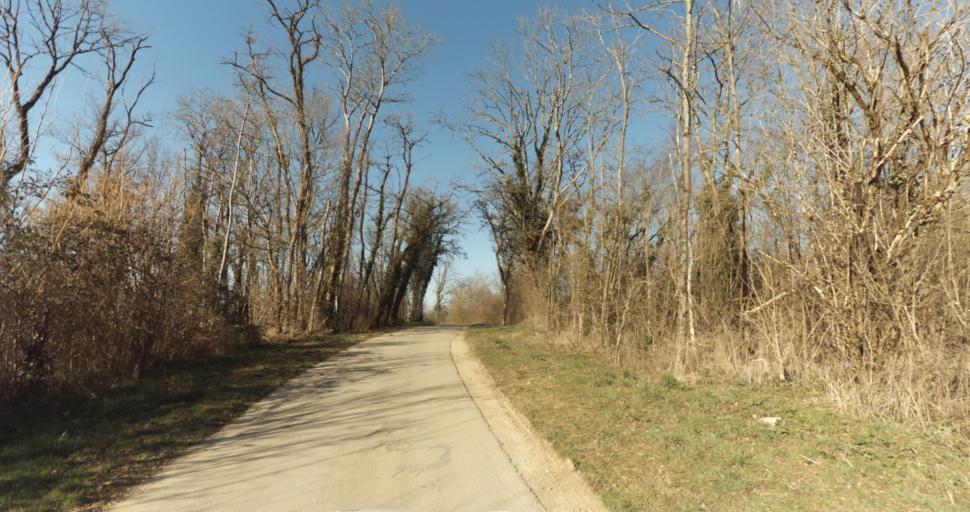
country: FR
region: Franche-Comte
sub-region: Departement du Jura
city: Montmorot
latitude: 46.7011
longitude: 5.5205
